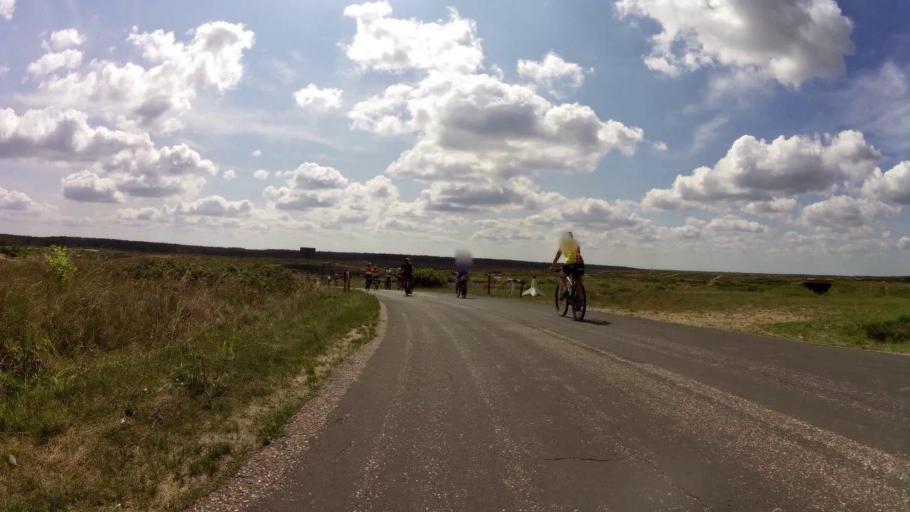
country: PL
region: West Pomeranian Voivodeship
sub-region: Powiat drawski
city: Drawsko Pomorskie
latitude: 53.4521
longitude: 15.7741
